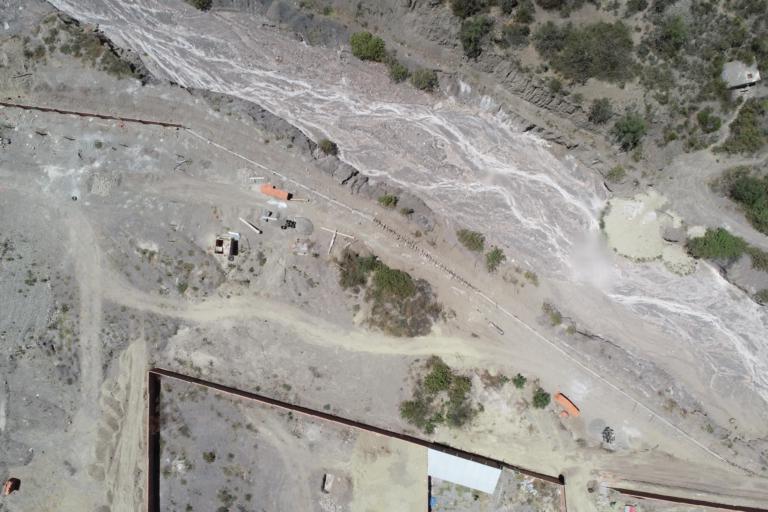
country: BO
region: La Paz
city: La Paz
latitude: -16.6450
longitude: -68.0396
